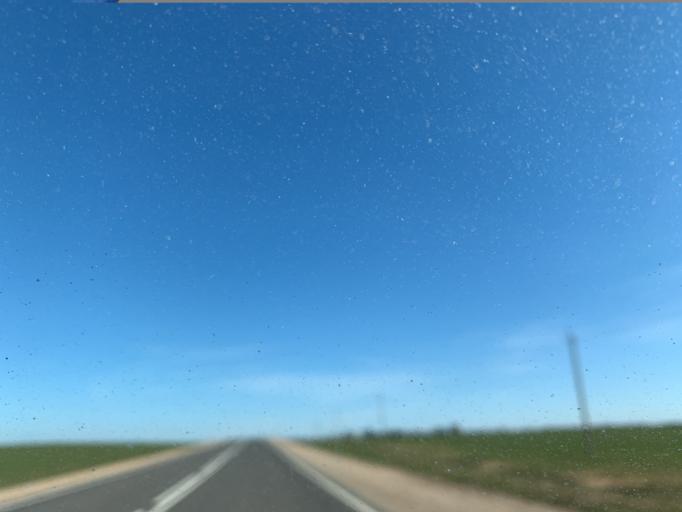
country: BY
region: Minsk
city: Nyasvizh
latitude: 53.2224
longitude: 26.7071
